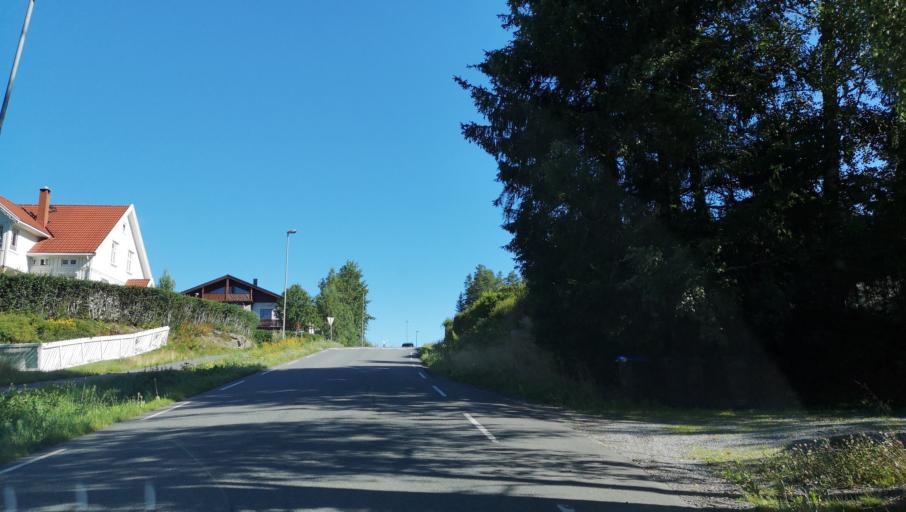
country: NO
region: Ostfold
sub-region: Hobol
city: Knappstad
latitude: 59.6276
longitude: 11.0269
